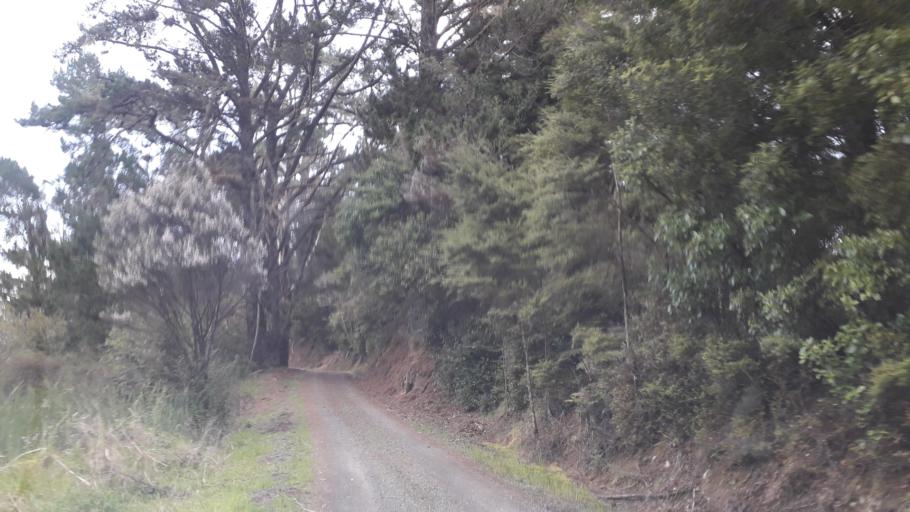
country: NZ
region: Northland
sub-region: Far North District
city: Waimate North
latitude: -35.3181
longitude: 173.5771
